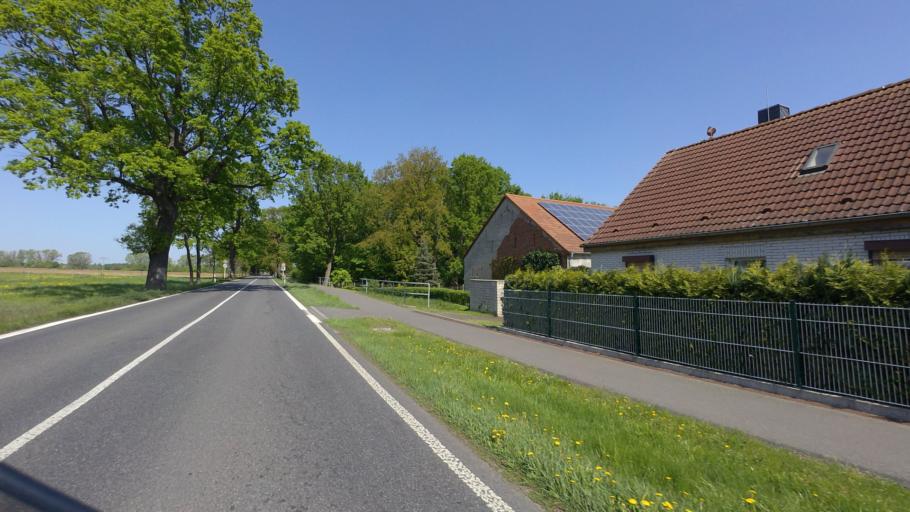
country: DE
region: Brandenburg
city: Beeskow
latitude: 52.1813
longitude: 14.2806
